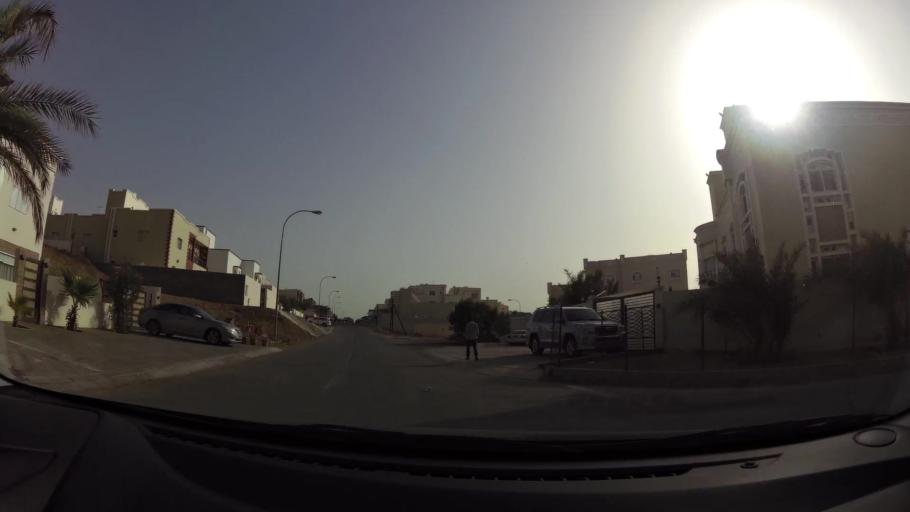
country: OM
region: Muhafazat Masqat
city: Bawshar
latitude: 23.5460
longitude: 58.3554
